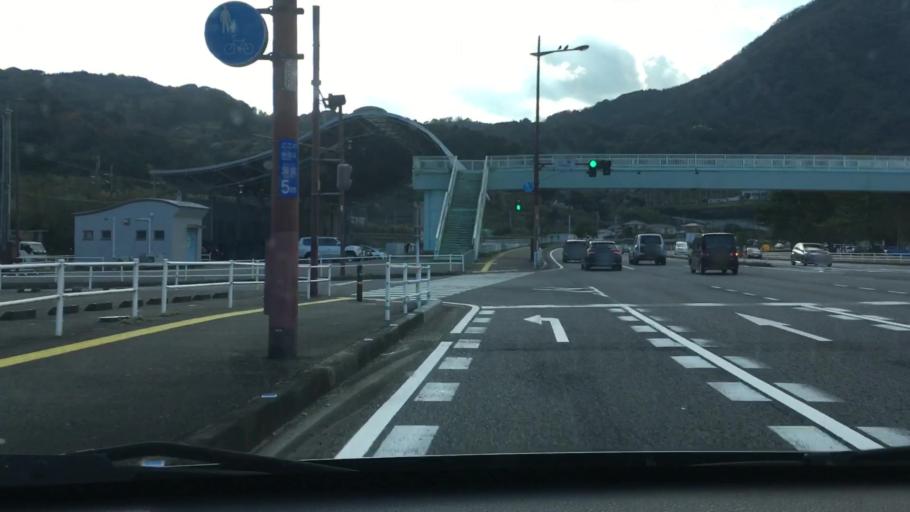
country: JP
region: Oita
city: Beppu
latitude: 33.2563
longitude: 131.5505
